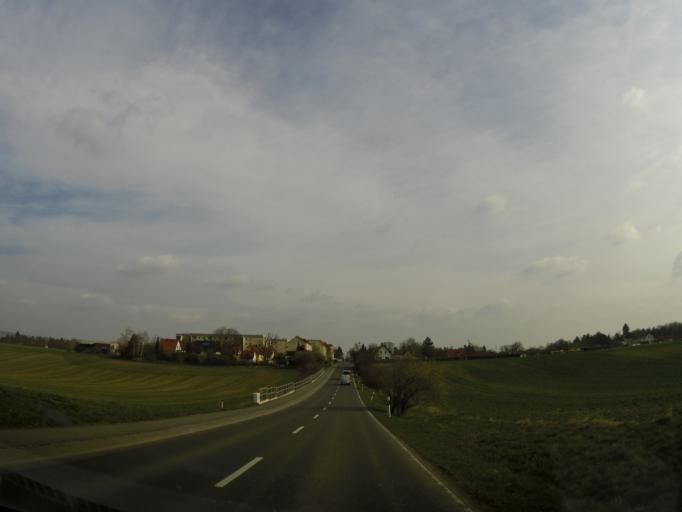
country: DE
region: Thuringia
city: Weimar
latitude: 50.9652
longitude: 11.3130
